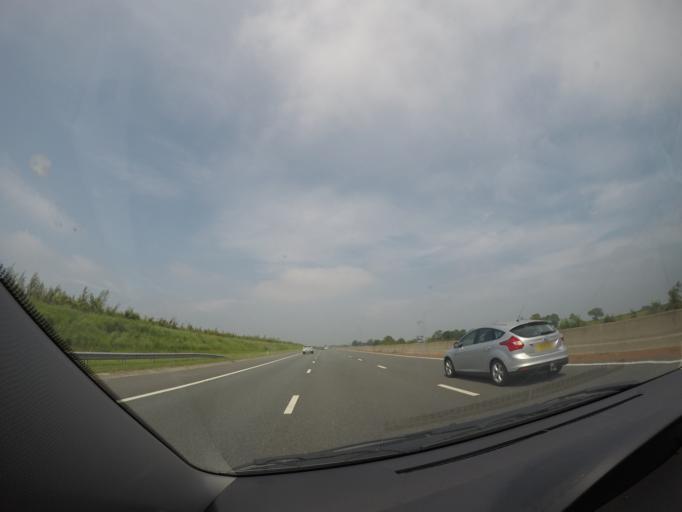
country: GB
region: England
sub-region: North Yorkshire
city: Bedale
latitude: 54.2604
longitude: -1.5159
